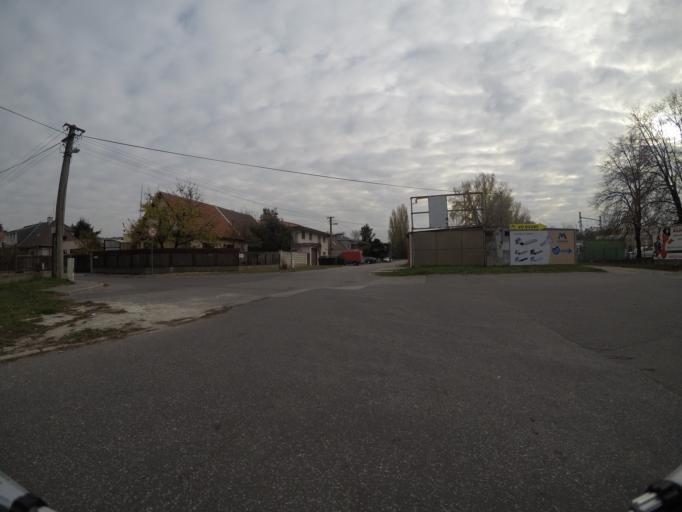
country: SK
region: Bratislavsky
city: Bratislava
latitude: 48.1675
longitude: 17.1592
